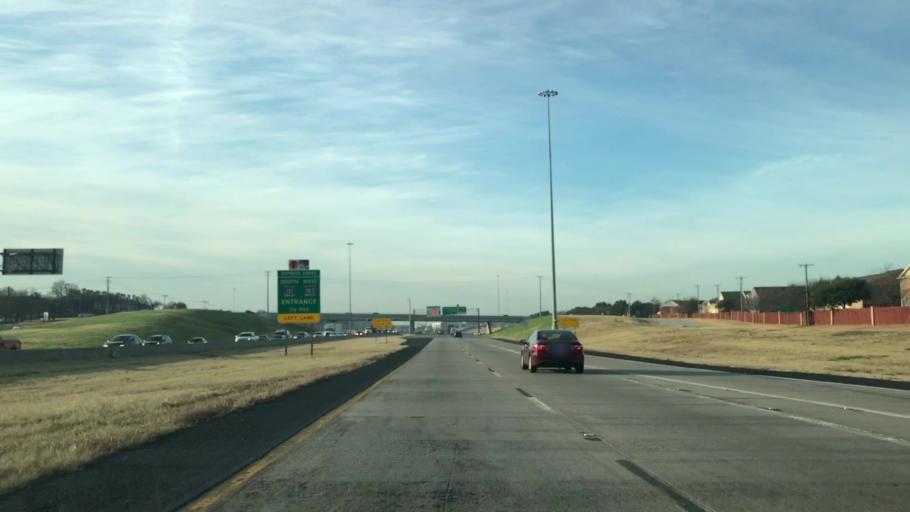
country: US
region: Texas
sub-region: Tarrant County
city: Bedford
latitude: 32.8477
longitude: -97.1139
